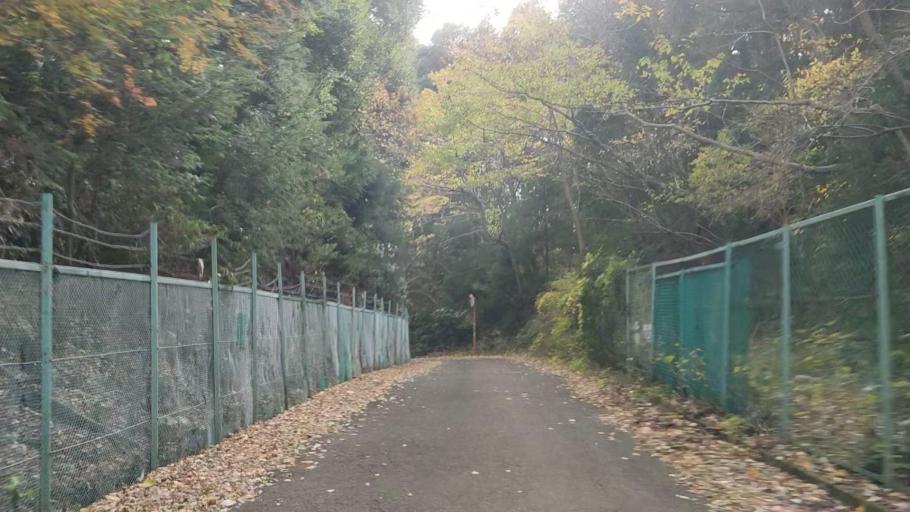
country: JP
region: Kanagawa
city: Minami-rinkan
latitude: 35.4820
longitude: 139.5008
